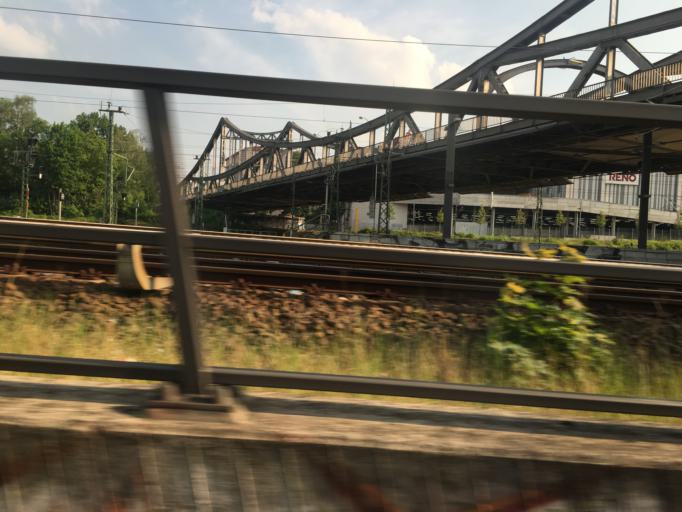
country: DE
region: Berlin
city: Gesundbrunnen
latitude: 52.5491
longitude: 13.3928
